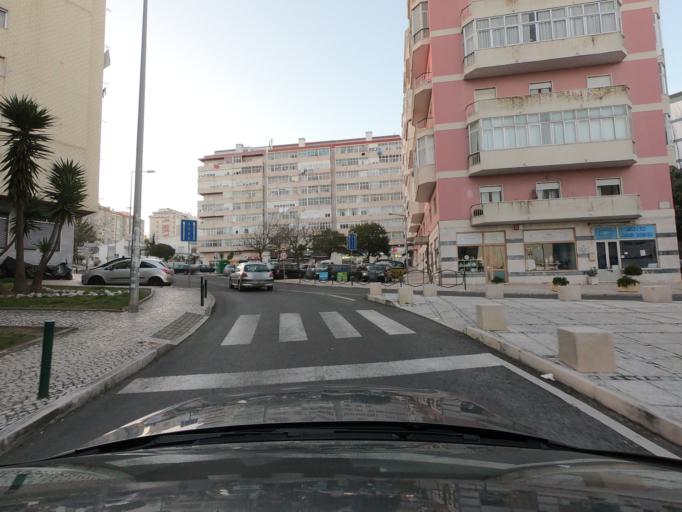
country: PT
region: Lisbon
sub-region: Sintra
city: Queluz
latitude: 38.7579
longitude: -9.2644
